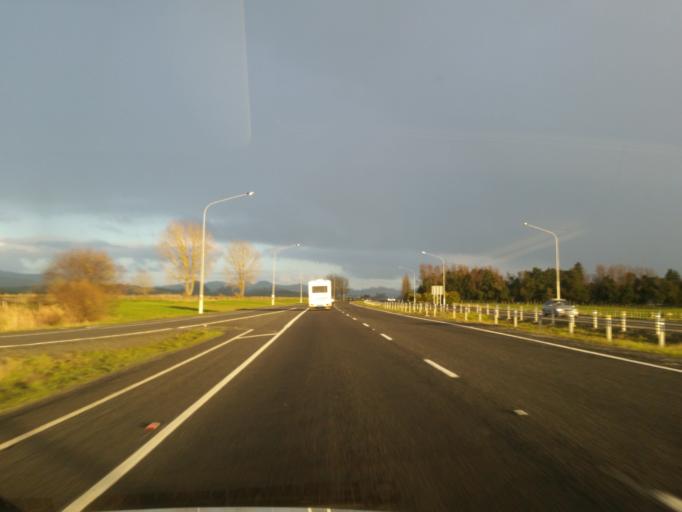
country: NZ
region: Waikato
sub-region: Waikato District
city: Te Kauwhata
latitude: -37.4917
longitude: 175.1615
